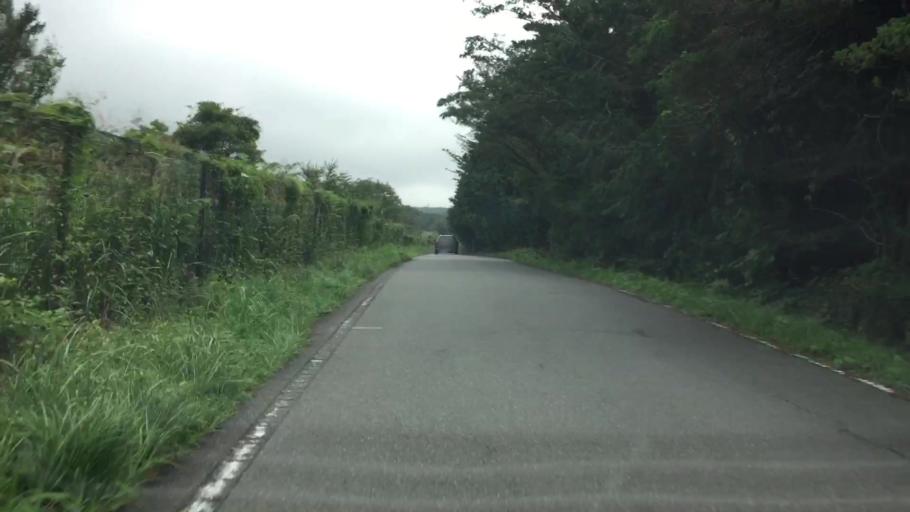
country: JP
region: Shizuoka
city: Fujinomiya
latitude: 35.3695
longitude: 138.5819
